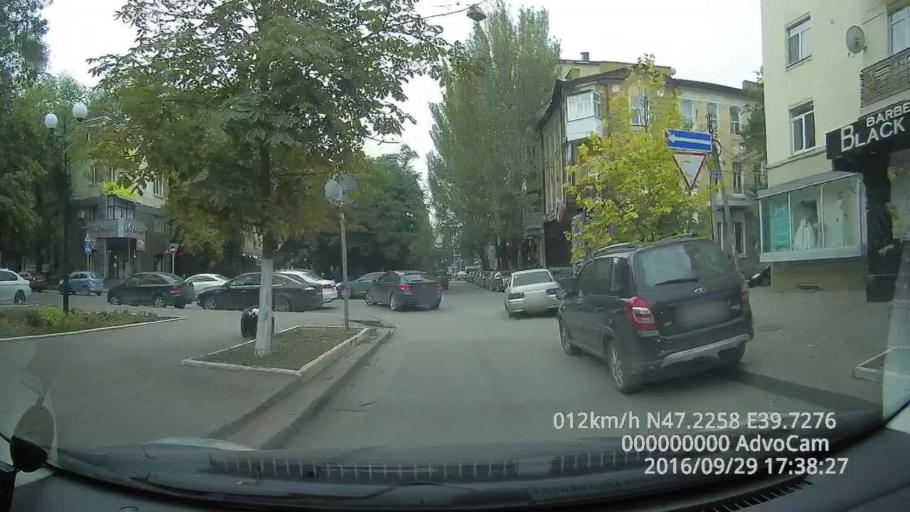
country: RU
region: Rostov
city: Rostov-na-Donu
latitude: 47.2259
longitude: 39.7275
